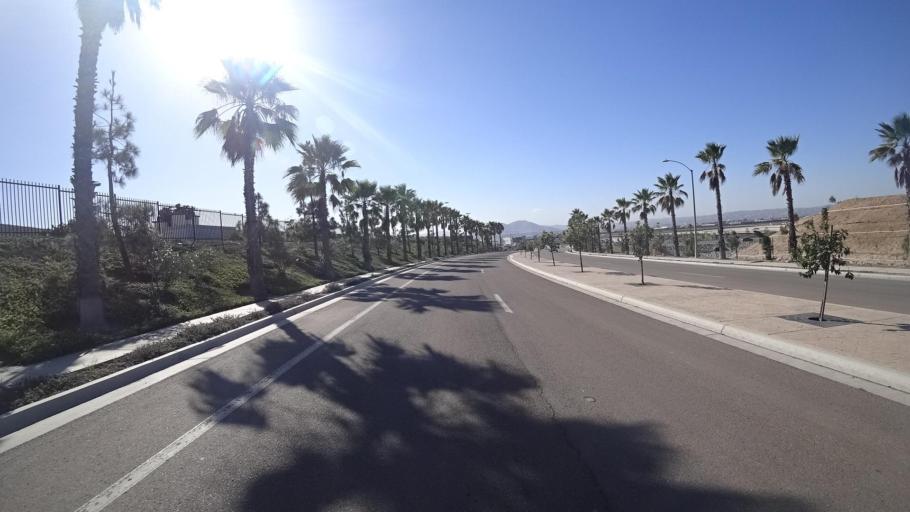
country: MX
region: Baja California
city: Tijuana
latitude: 32.5689
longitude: -116.9129
